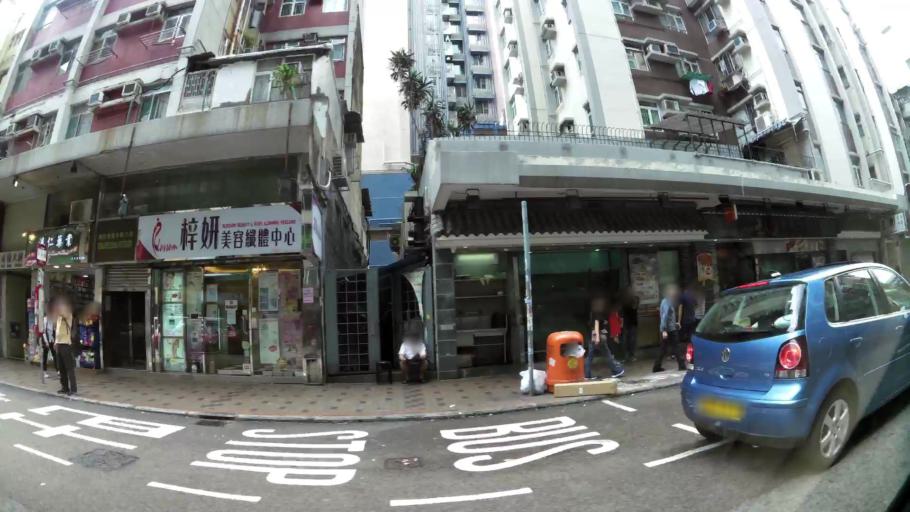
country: HK
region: Sham Shui Po
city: Sham Shui Po
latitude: 22.3355
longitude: 114.1591
